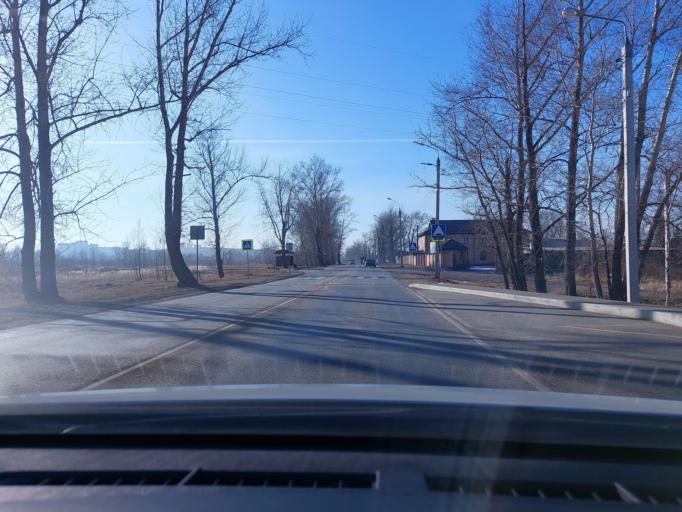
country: RU
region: Irkutsk
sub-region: Irkutskiy Rayon
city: Irkutsk
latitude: 52.3069
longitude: 104.2562
